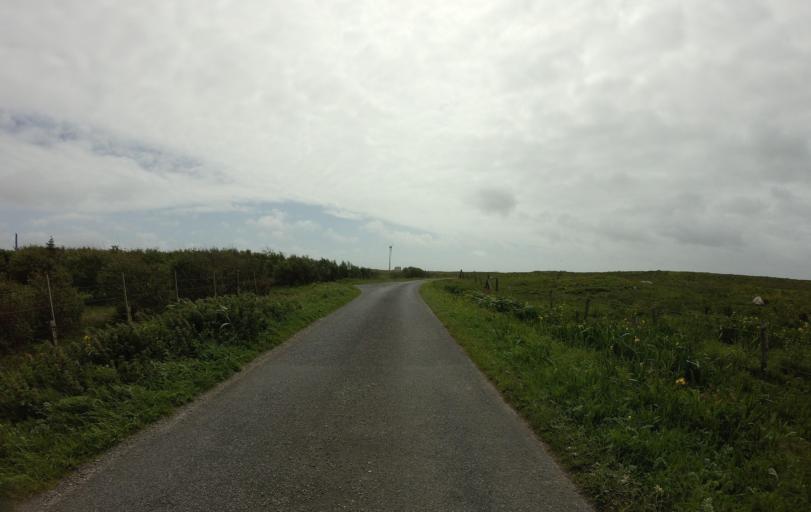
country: GB
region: Scotland
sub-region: Eilean Siar
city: Isle of South Uist
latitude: 57.2461
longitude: -7.4046
